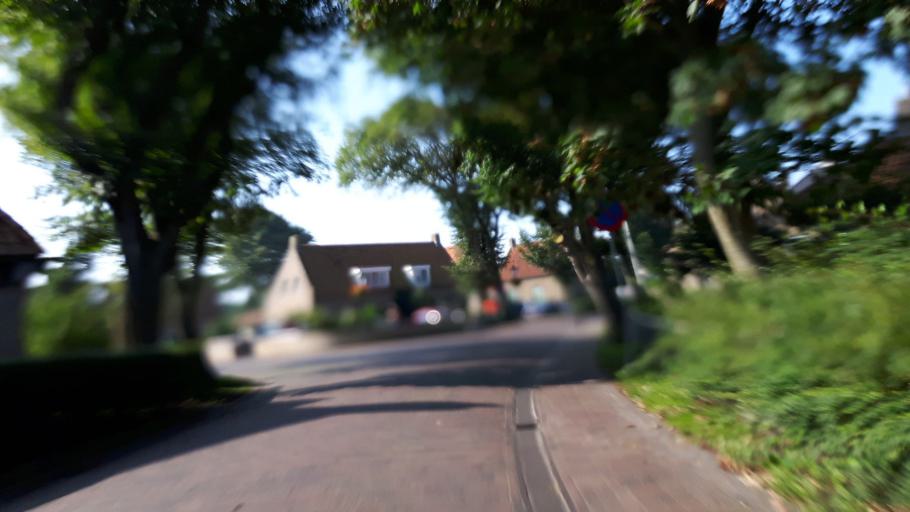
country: NL
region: Friesland
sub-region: Gemeente Ameland
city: Nes
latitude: 53.4477
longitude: 5.7997
